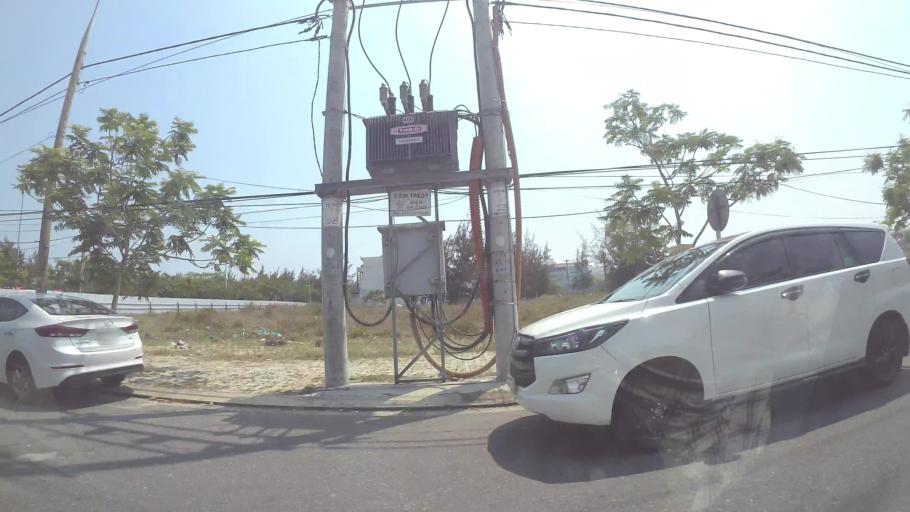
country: VN
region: Da Nang
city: Ngu Hanh Son
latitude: 16.0005
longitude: 108.2669
